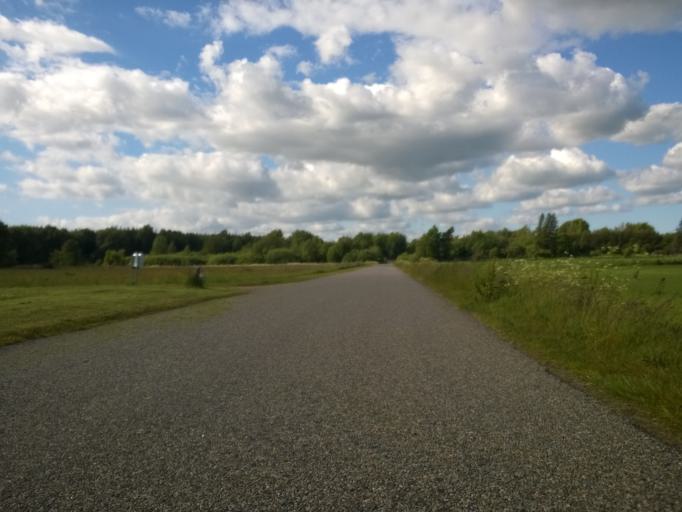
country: DK
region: Central Jutland
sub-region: Holstebro Kommune
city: Vinderup
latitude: 56.5063
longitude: 8.8478
